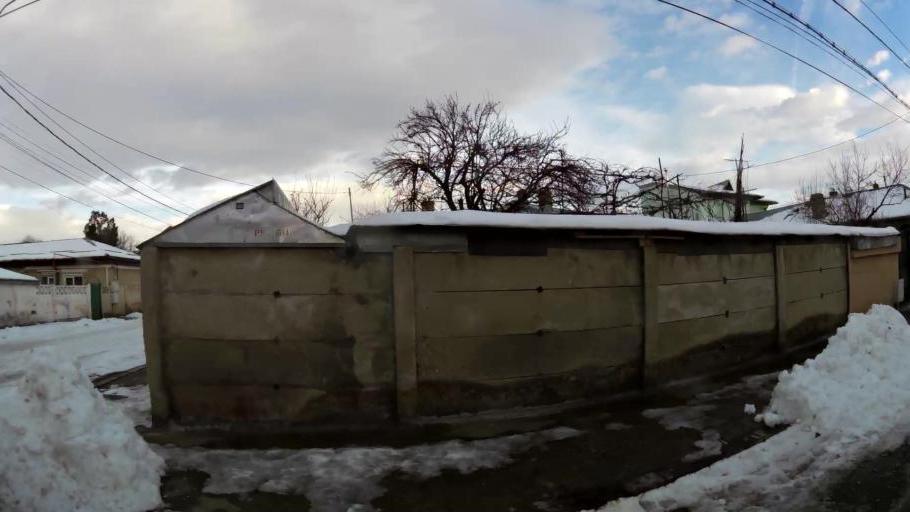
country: RO
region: Ilfov
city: Dobroesti
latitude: 44.4538
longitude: 26.1830
